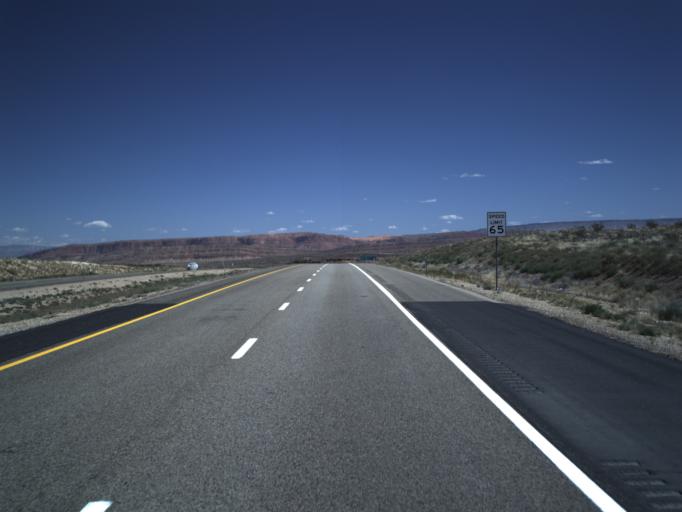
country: US
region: Utah
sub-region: Washington County
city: Saint George
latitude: 37.0026
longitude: -113.5464
